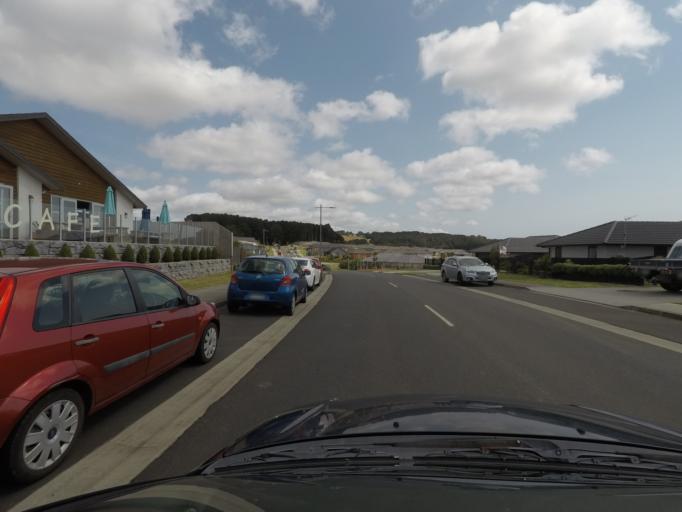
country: NZ
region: Northland
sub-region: Whangarei
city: Whangarei
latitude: -35.6787
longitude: 174.3170
